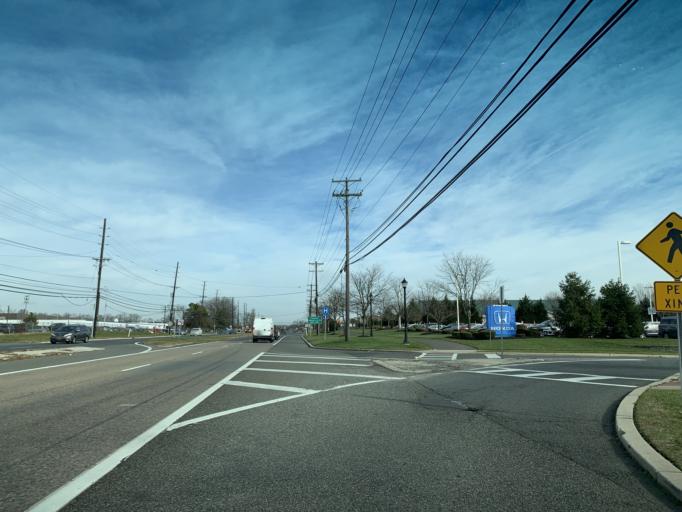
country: US
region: New Jersey
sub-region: Mercer County
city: Yardville
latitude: 40.1908
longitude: -74.6496
